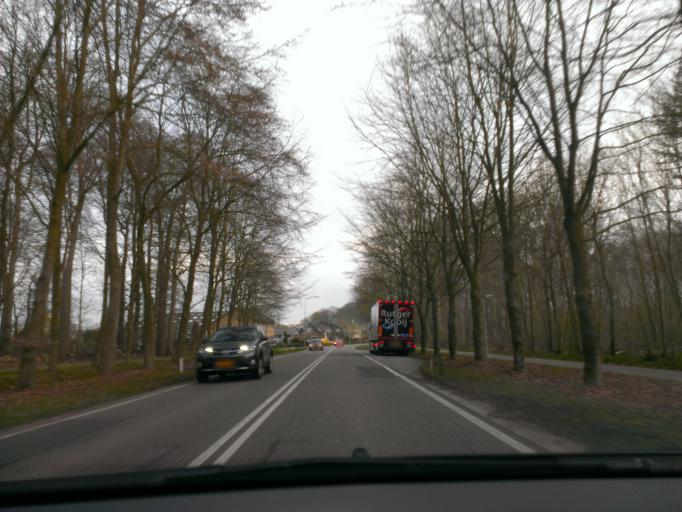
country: NL
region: Gelderland
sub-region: Gemeente Voorst
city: Twello
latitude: 52.2236
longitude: 6.1117
